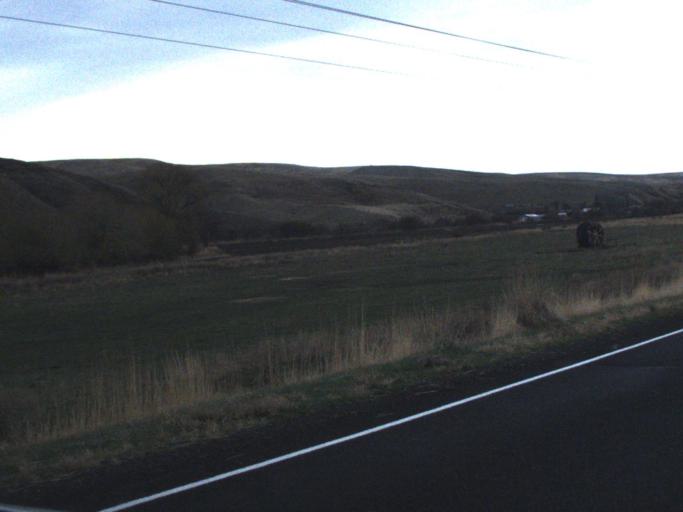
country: US
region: Washington
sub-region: Columbia County
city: Dayton
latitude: 46.5100
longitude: -118.0904
